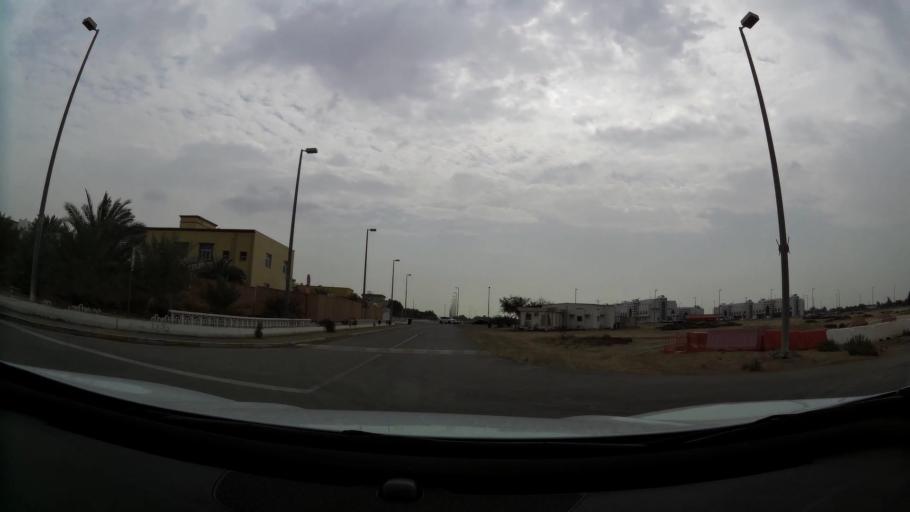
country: AE
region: Abu Dhabi
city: Abu Dhabi
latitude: 24.6287
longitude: 54.7127
